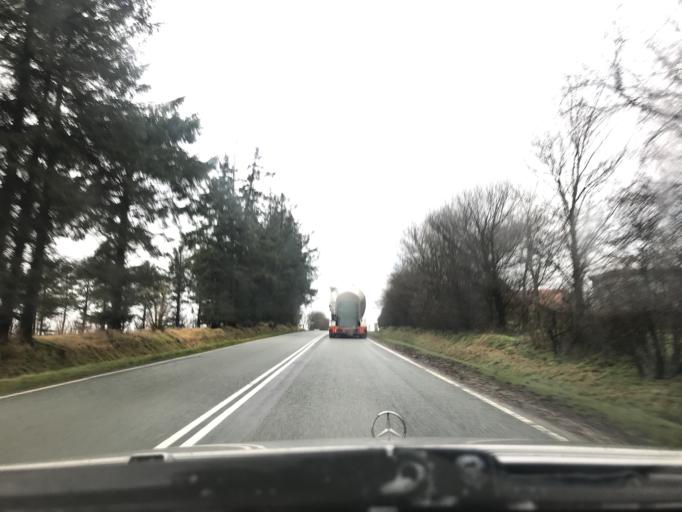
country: DK
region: South Denmark
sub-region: Esbjerg Kommune
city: Ribe
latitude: 55.2719
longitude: 8.8704
